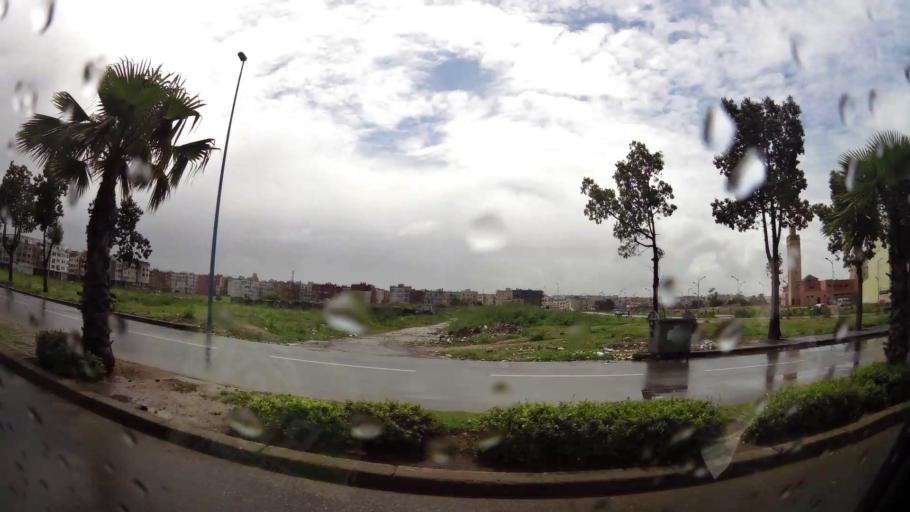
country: MA
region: Grand Casablanca
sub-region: Casablanca
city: Casablanca
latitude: 33.5495
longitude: -7.6778
